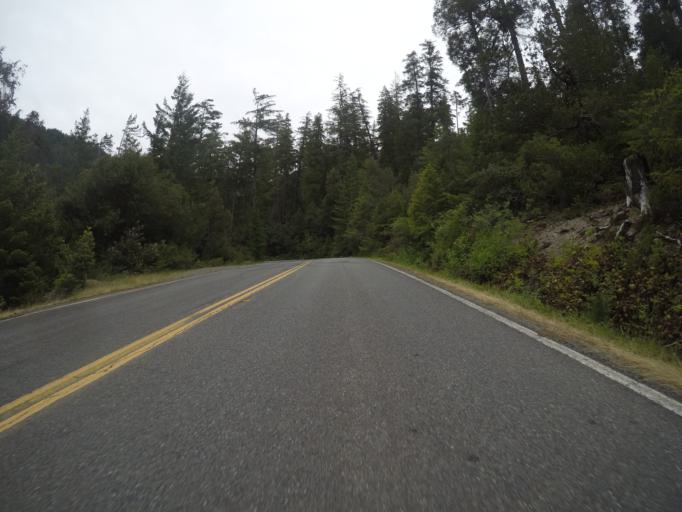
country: US
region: California
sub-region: Del Norte County
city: Bertsch-Oceanview
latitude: 41.7027
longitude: -123.9367
